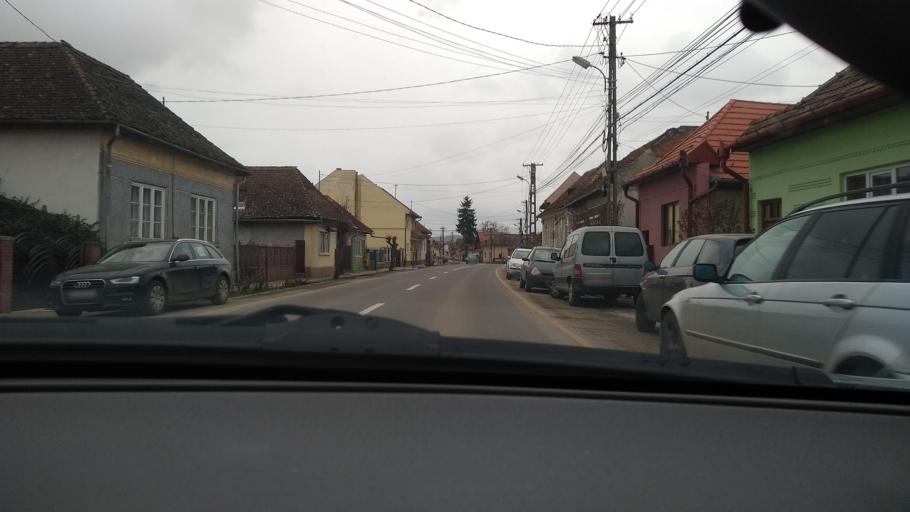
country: RO
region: Mures
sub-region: Comuna Miercurea Nirajului
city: Miercurea Nirajului
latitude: 46.5363
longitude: 24.8063
